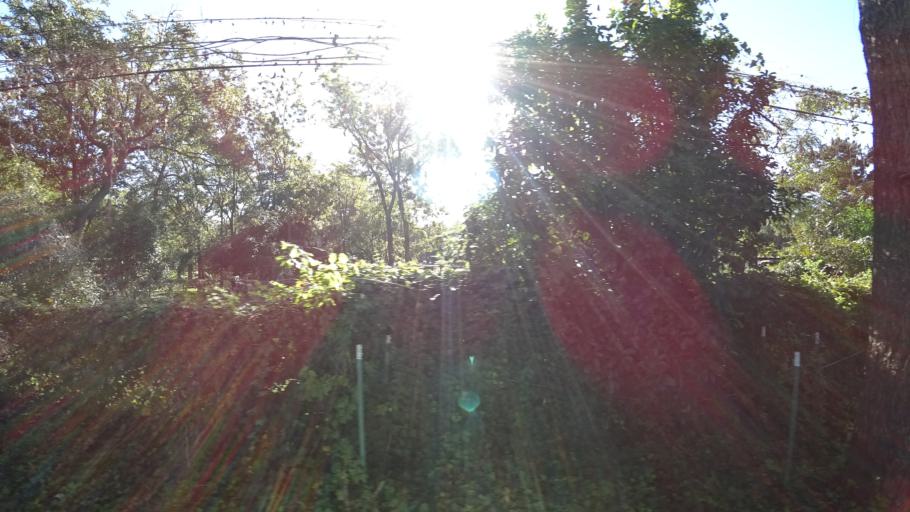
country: US
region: Texas
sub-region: Travis County
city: West Lake Hills
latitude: 30.3423
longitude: -97.7914
